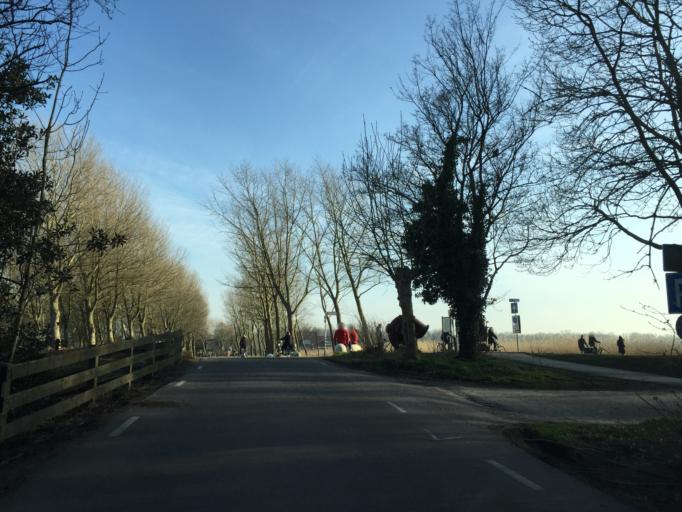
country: NL
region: South Holland
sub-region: Gemeente Den Haag
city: Ypenburg
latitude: 52.0218
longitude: 4.3878
